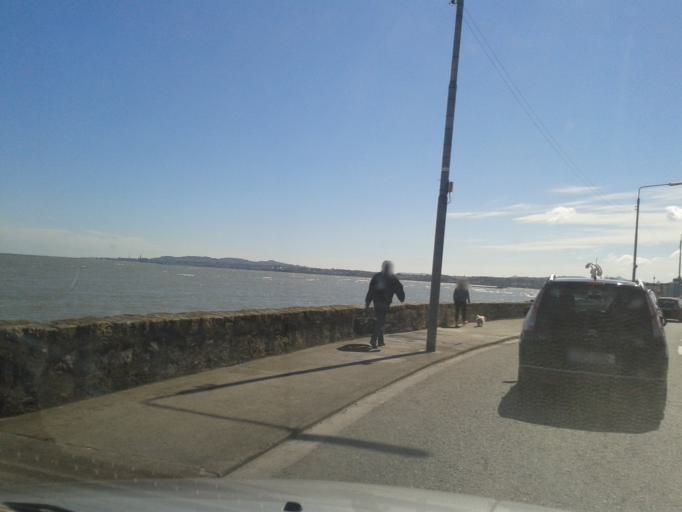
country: IE
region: Leinster
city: Sandymount
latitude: 53.3302
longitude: -6.2090
